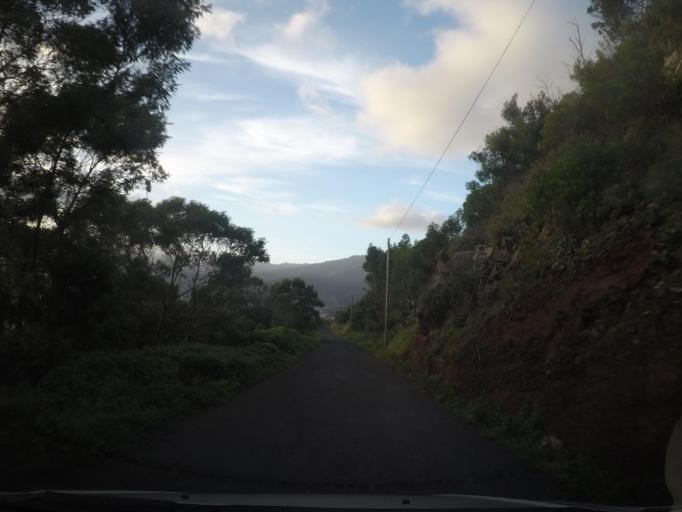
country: PT
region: Madeira
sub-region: Machico
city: Canical
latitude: 32.7258
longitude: -16.7596
